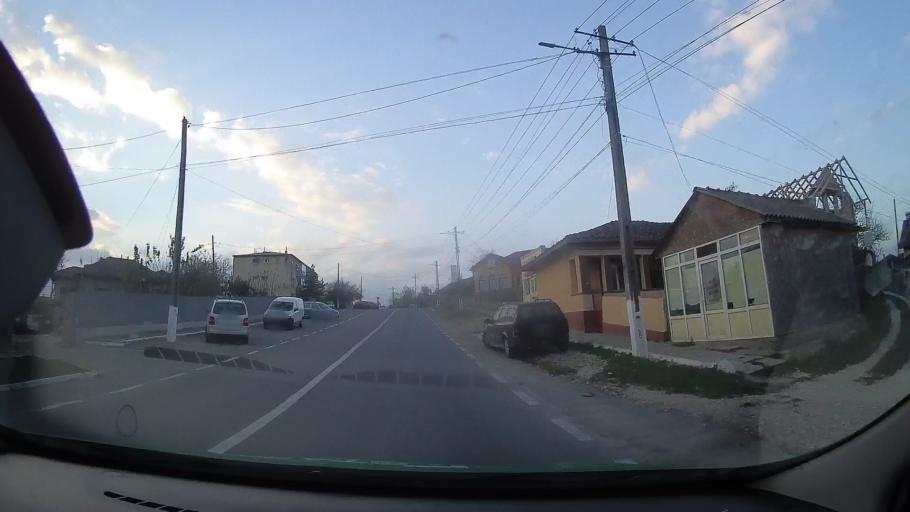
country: RO
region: Constanta
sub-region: Comuna Baneasa
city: Baneasa
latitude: 44.0636
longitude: 27.7016
